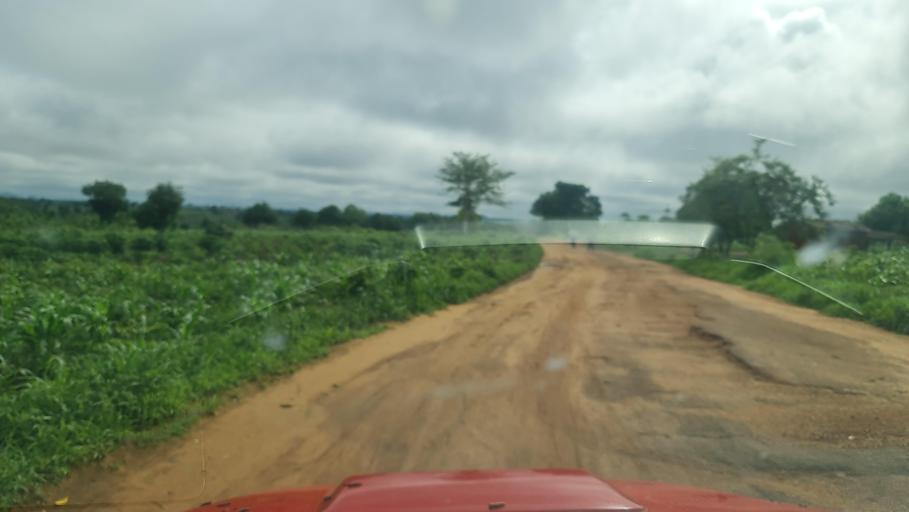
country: MW
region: Southern Region
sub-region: Nsanje District
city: Nsanje
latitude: -17.2225
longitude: 35.6647
